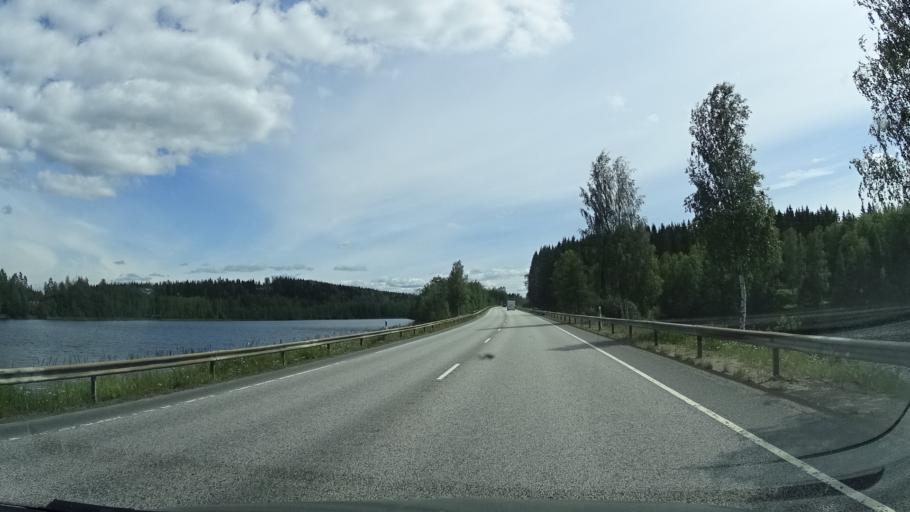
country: FI
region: Central Finland
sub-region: Jyvaeskylae
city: Jyvaeskylae
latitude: 62.2573
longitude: 25.6141
